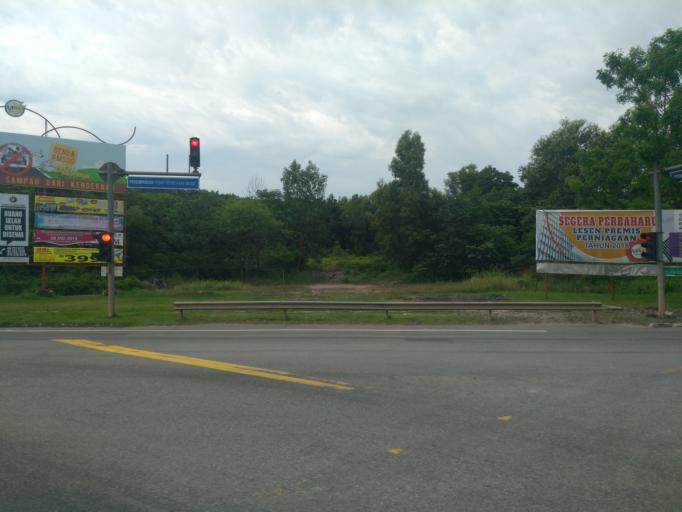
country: MY
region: Melaka
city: Kampung Ayer Keroh
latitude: 2.2856
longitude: 102.2701
